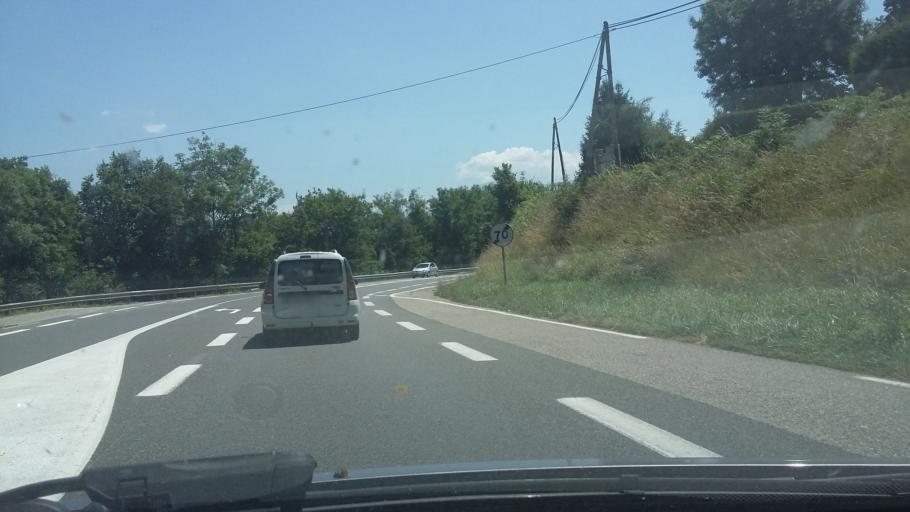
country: FR
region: Rhone-Alpes
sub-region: Departement de la Savoie
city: Le Bourget-du-Lac
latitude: 45.6758
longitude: 5.8529
